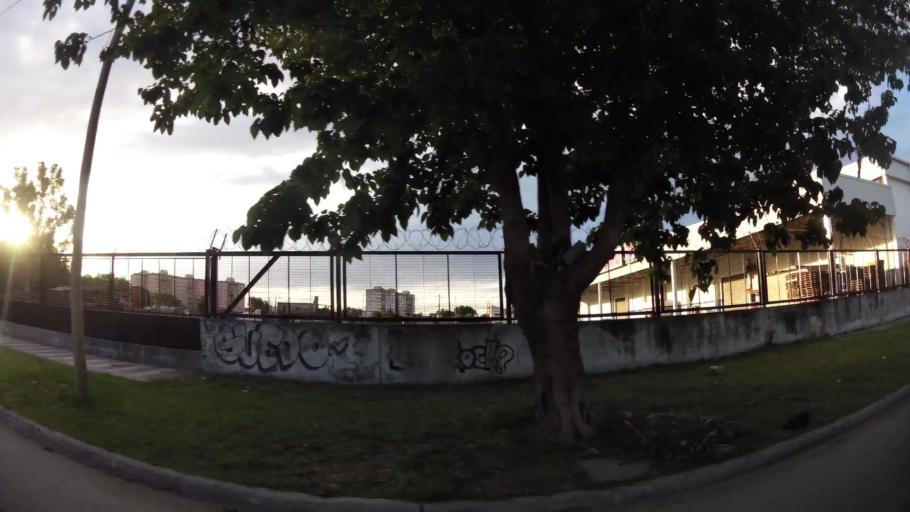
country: AR
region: Buenos Aires
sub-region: Partido de Avellaneda
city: Avellaneda
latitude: -34.7045
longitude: -58.3405
